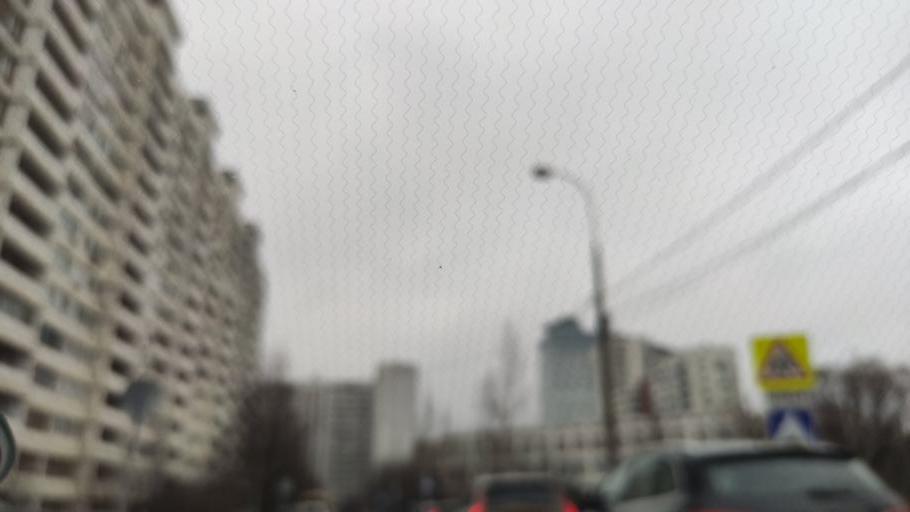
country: RU
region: Moskovskaya
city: Bol'shaya Setun'
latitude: 55.7443
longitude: 37.4300
